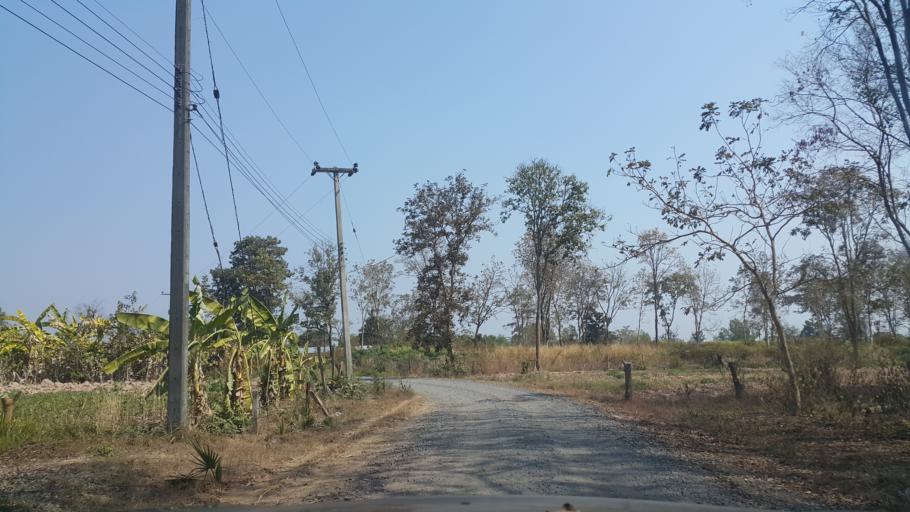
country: TH
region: Buriram
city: Krasang
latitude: 15.1051
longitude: 103.3764
